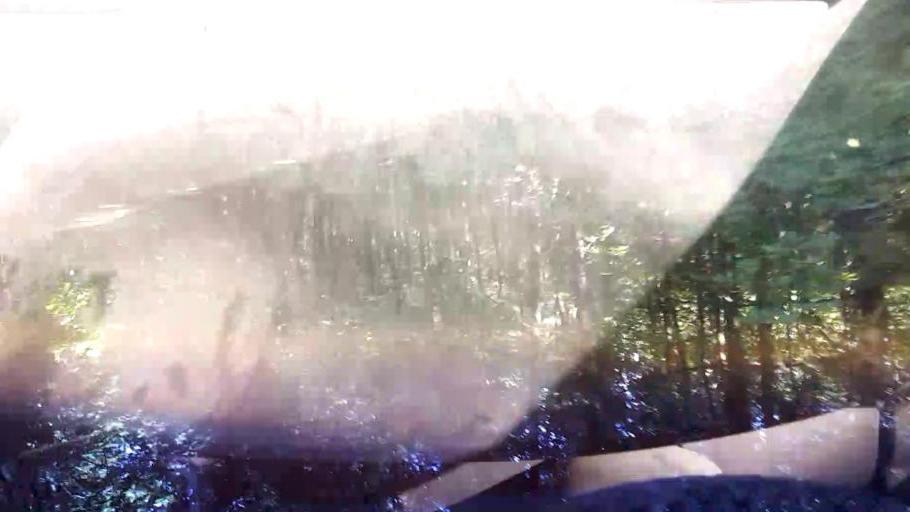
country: DE
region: Bavaria
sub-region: Upper Franconia
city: Litzendorf
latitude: 49.8828
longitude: 11.0340
